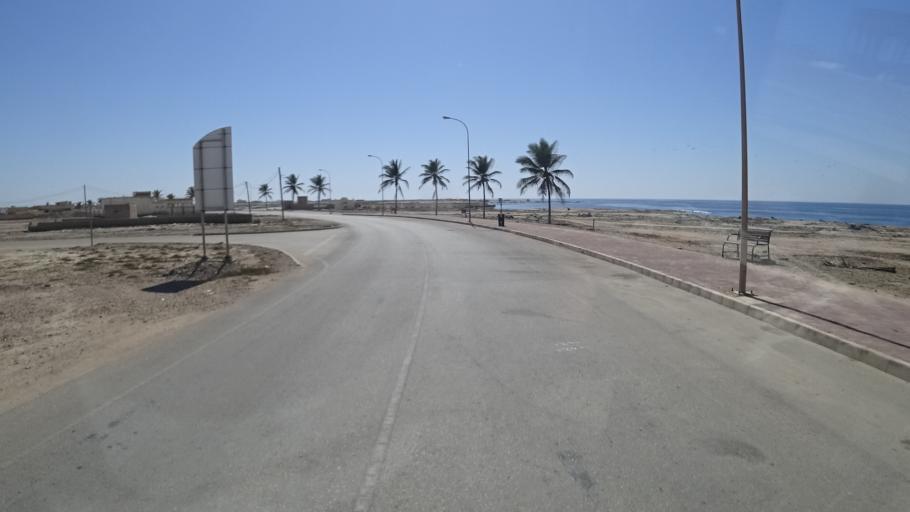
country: OM
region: Zufar
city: Salalah
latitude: 16.9777
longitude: 54.6887
